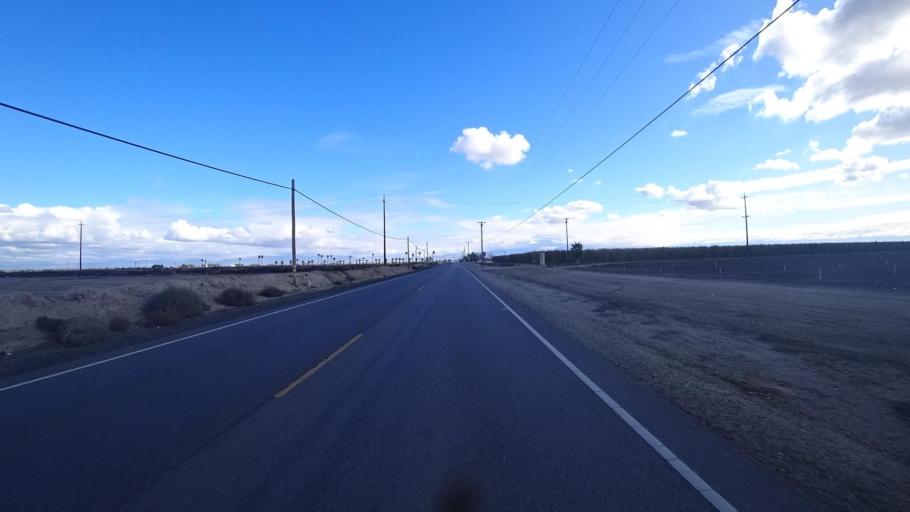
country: US
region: California
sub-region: Kern County
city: Greenfield
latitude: 35.2671
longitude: -119.0979
